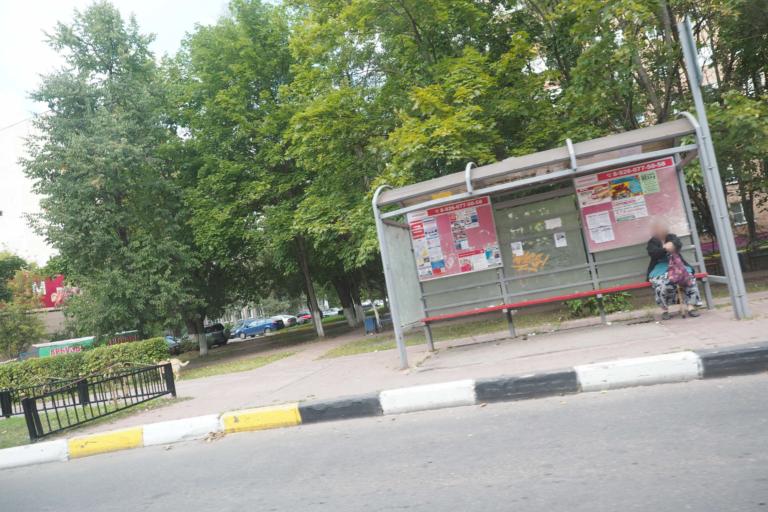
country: RU
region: Moskovskaya
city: Kratovo
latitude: 55.5905
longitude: 38.2079
